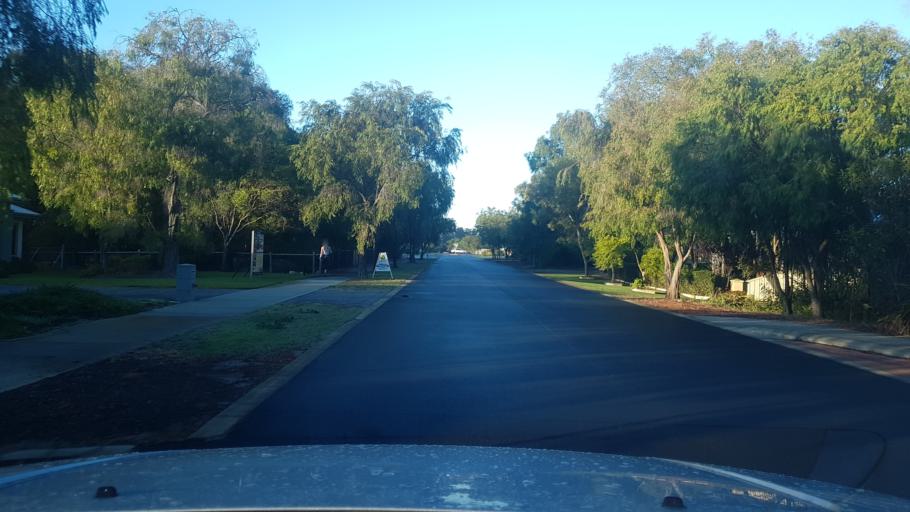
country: AU
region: Western Australia
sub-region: Busselton
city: Vasse
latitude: -33.6622
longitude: 115.2626
